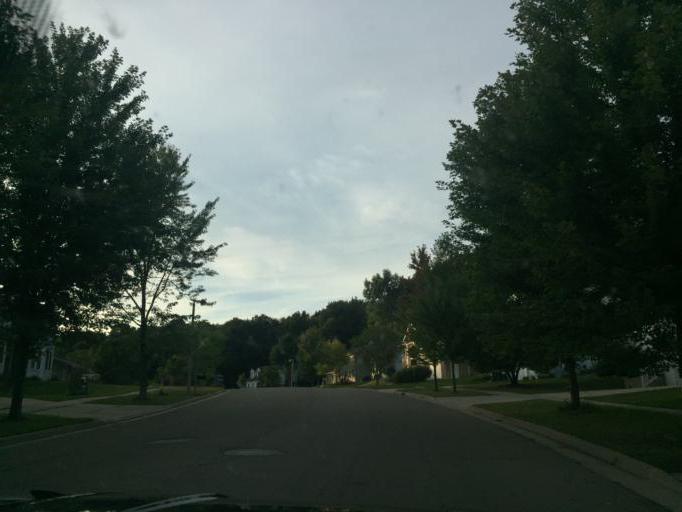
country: US
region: Minnesota
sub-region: Olmsted County
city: Rochester
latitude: 44.0092
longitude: -92.4929
